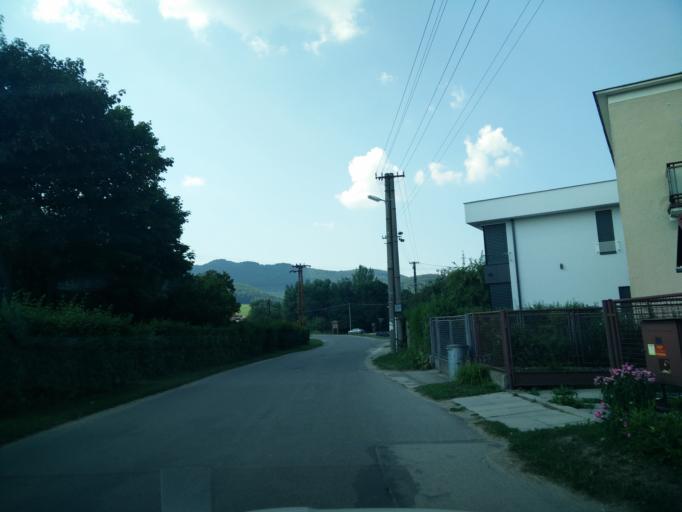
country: SK
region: Zilinsky
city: Rajec
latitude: 49.1071
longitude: 18.6431
